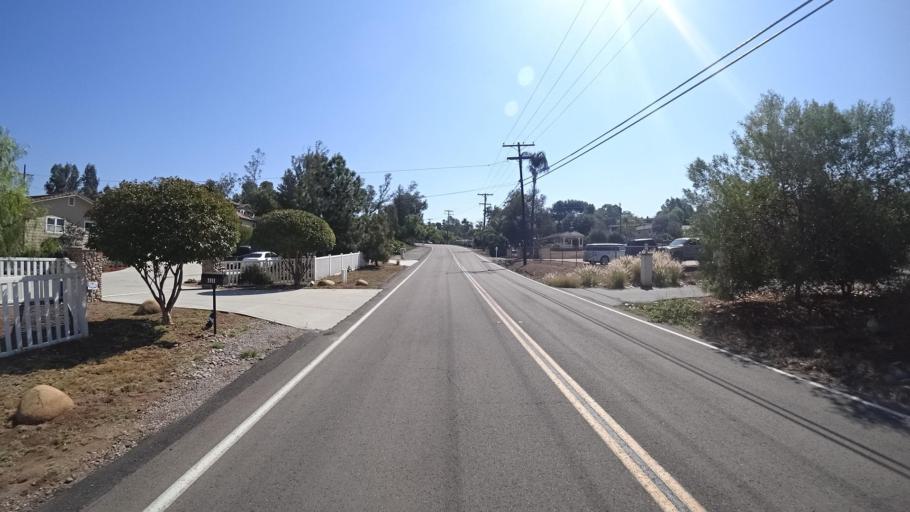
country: US
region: California
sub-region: San Diego County
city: Granite Hills
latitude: 32.7919
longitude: -116.9085
